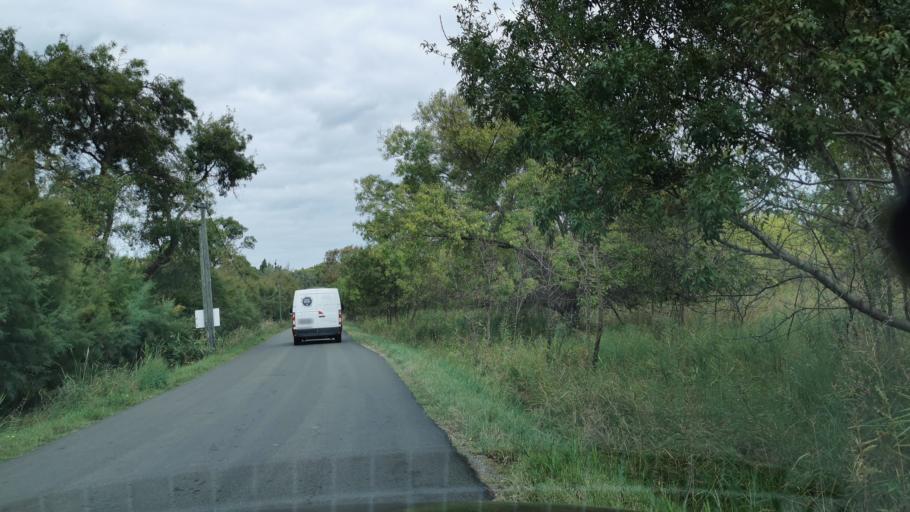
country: FR
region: Languedoc-Roussillon
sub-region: Departement de l'Herault
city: Lespignan
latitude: 43.2250
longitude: 3.1942
